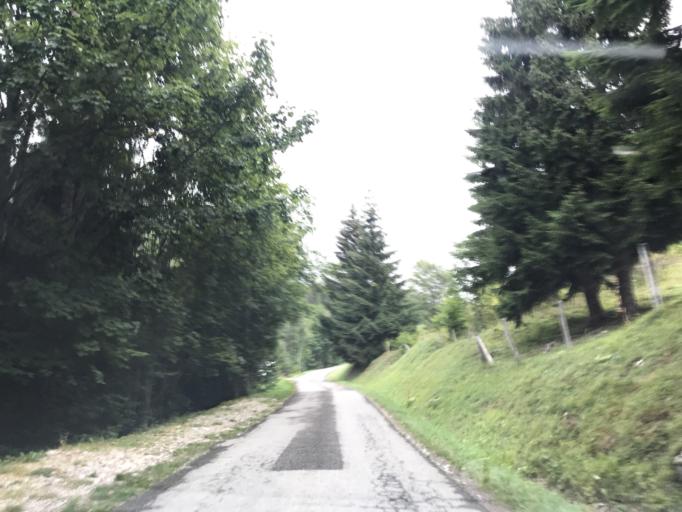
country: FR
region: Rhone-Alpes
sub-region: Departement de la Haute-Savoie
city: Talloires
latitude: 45.8189
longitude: 6.2612
